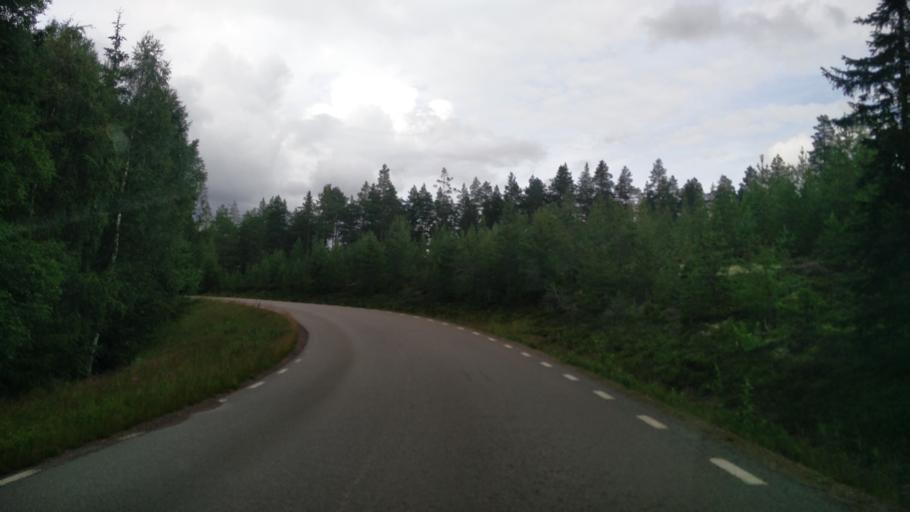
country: NO
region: Hedmark
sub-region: Trysil
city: Innbygda
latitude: 61.1599
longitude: 12.8211
